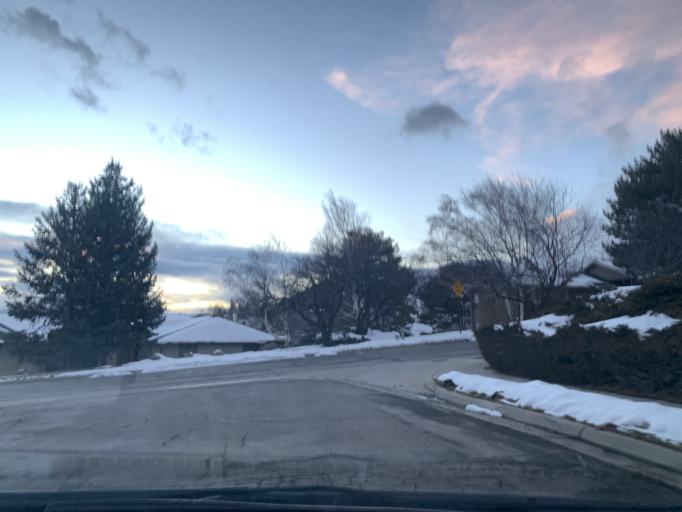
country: US
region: Utah
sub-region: Salt Lake County
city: Salt Lake City
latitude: 40.7845
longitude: -111.8519
